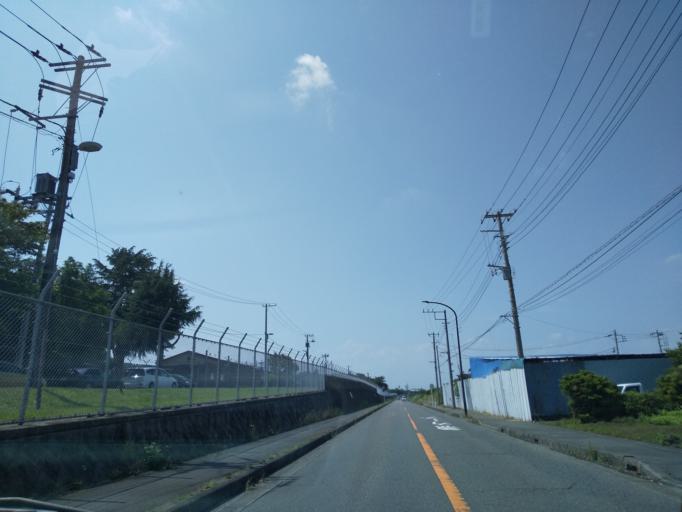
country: JP
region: Kanagawa
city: Zama
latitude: 35.5123
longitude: 139.3984
